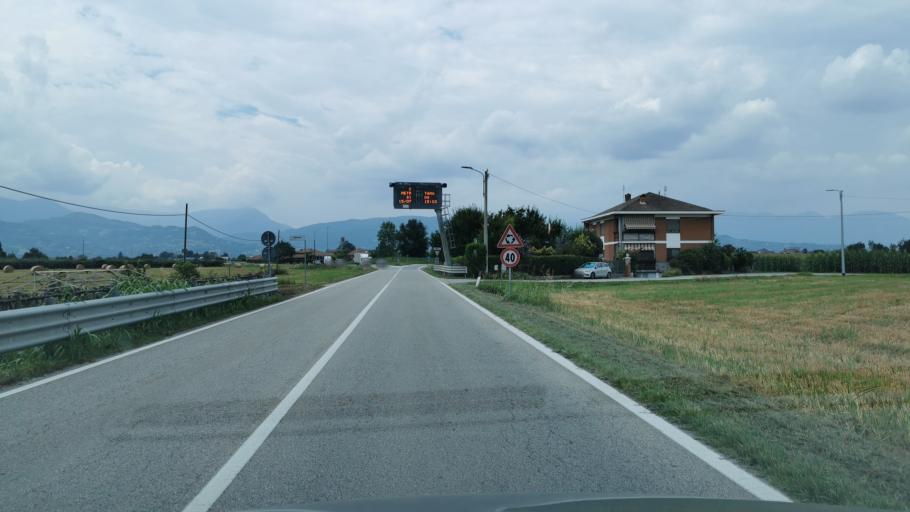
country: IT
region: Piedmont
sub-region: Provincia di Torino
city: Osasco
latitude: 44.8420
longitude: 7.3530
